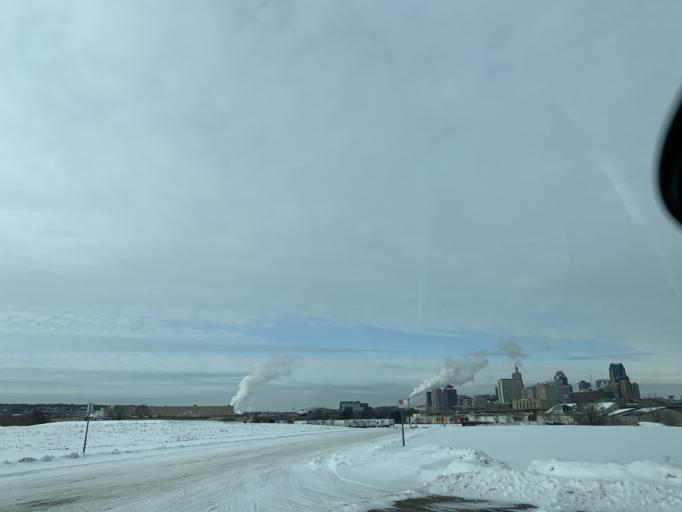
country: US
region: Minnesota
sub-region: Ramsey County
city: Saint Paul
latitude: 44.9444
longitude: -93.0683
